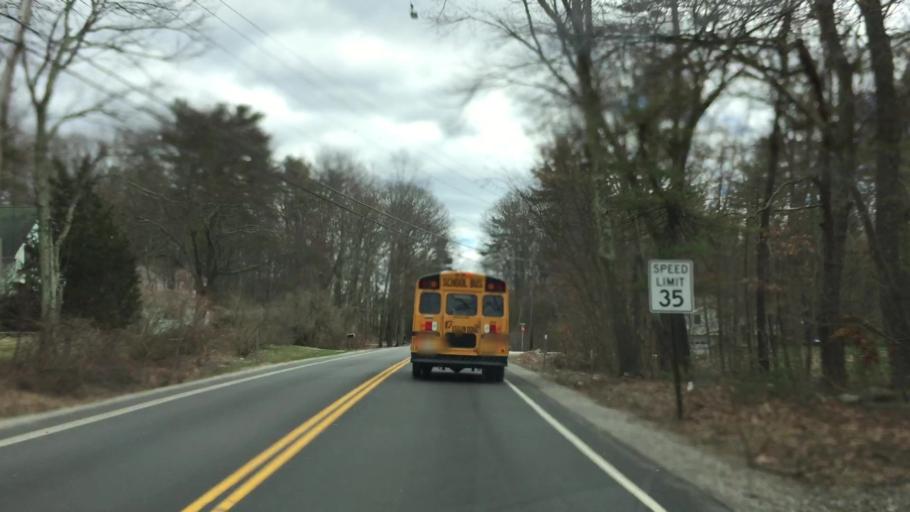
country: US
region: New Hampshire
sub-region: Rockingham County
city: Londonderry
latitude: 42.8174
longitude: -71.3610
